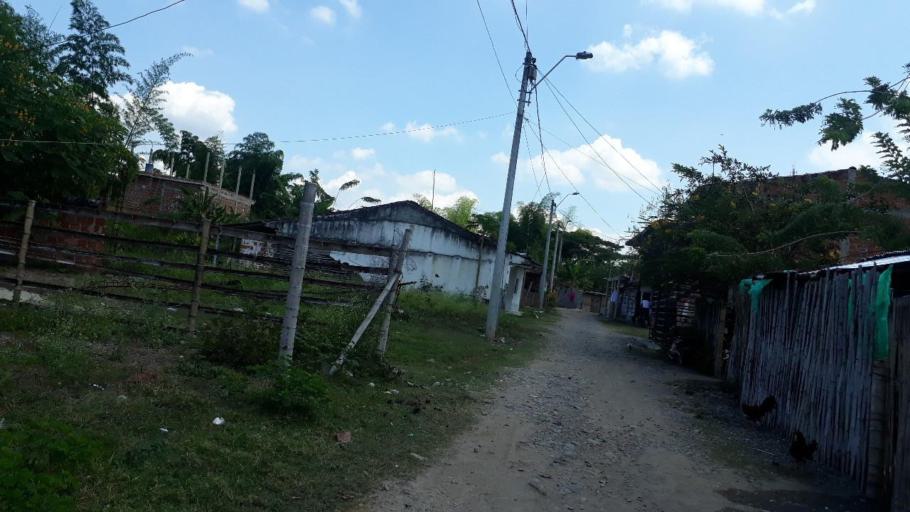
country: CO
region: Valle del Cauca
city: Jamundi
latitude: 3.1325
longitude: -76.5458
